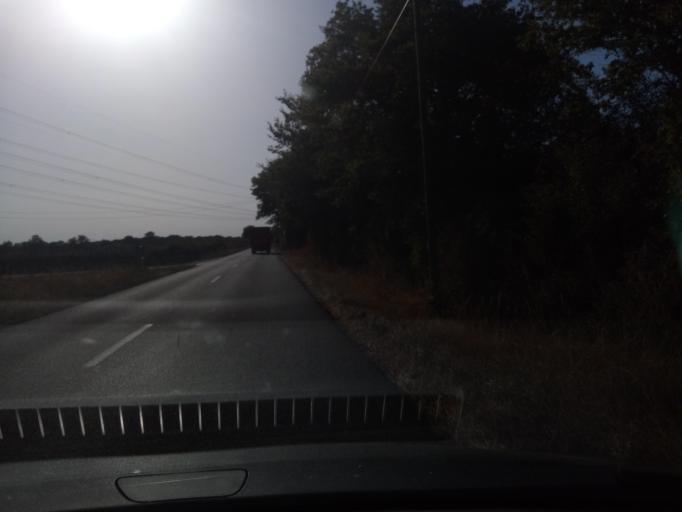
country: FR
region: Poitou-Charentes
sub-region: Departement de la Vienne
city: Montmorillon
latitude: 46.4463
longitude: 0.9787
